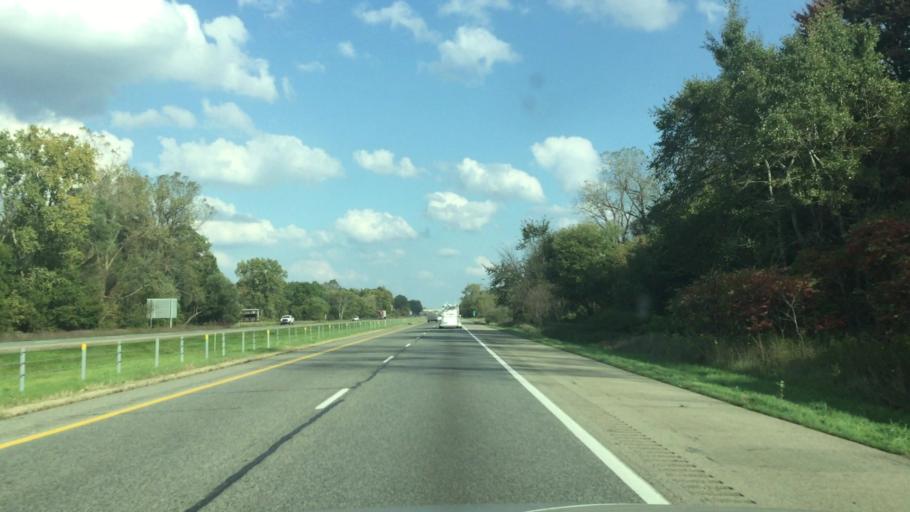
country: US
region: Michigan
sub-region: Calhoun County
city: Brownlee Park
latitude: 42.2976
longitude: -85.0555
